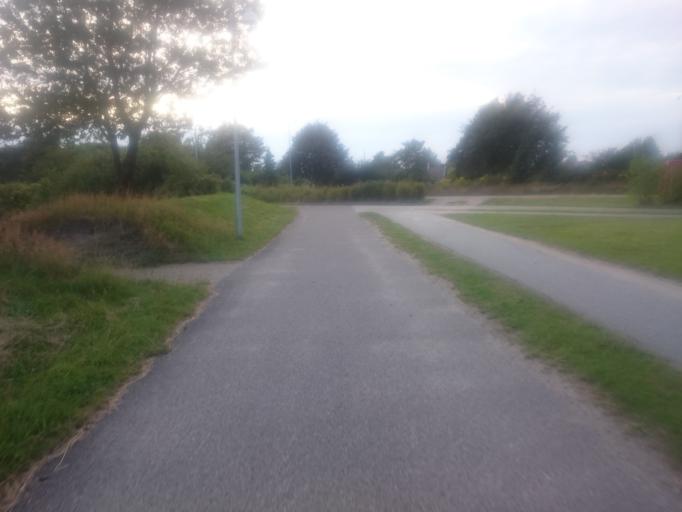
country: DK
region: South Denmark
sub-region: Billund Kommune
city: Billund
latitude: 55.7246
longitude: 9.1021
